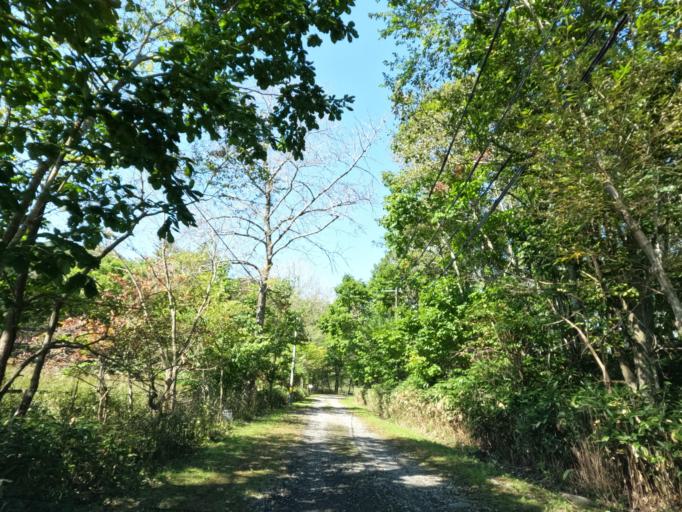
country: JP
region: Hokkaido
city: Muroran
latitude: 42.3915
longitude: 141.0307
